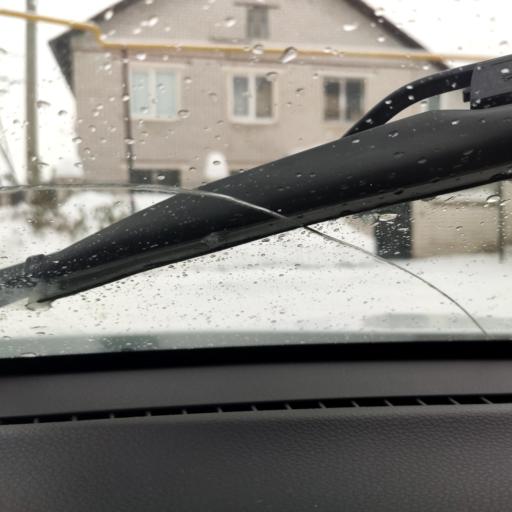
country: RU
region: Tatarstan
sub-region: Gorod Kazan'
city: Kazan
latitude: 55.7261
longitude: 49.1627
